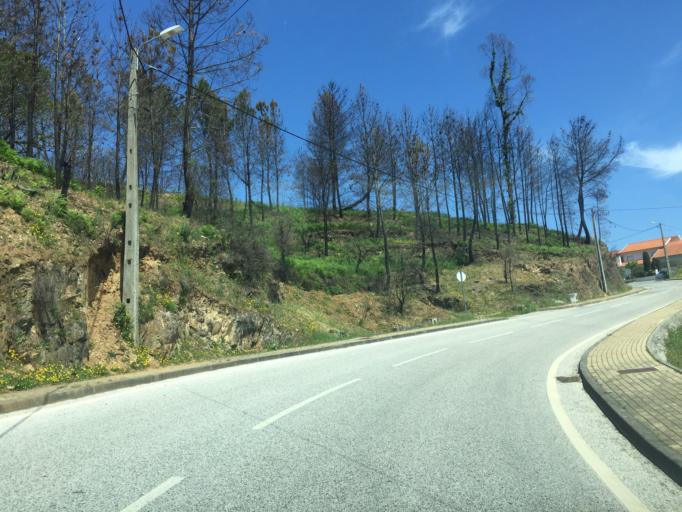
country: PT
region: Coimbra
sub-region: Pampilhosa da Serra
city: Pampilhosa da Serra
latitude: 40.0434
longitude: -7.9520
